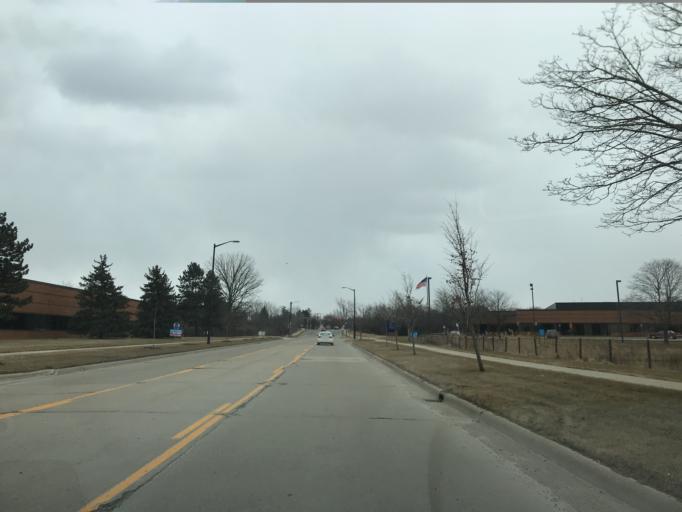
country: US
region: Michigan
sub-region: Washtenaw County
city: Ann Arbor
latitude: 42.2470
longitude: -83.7309
